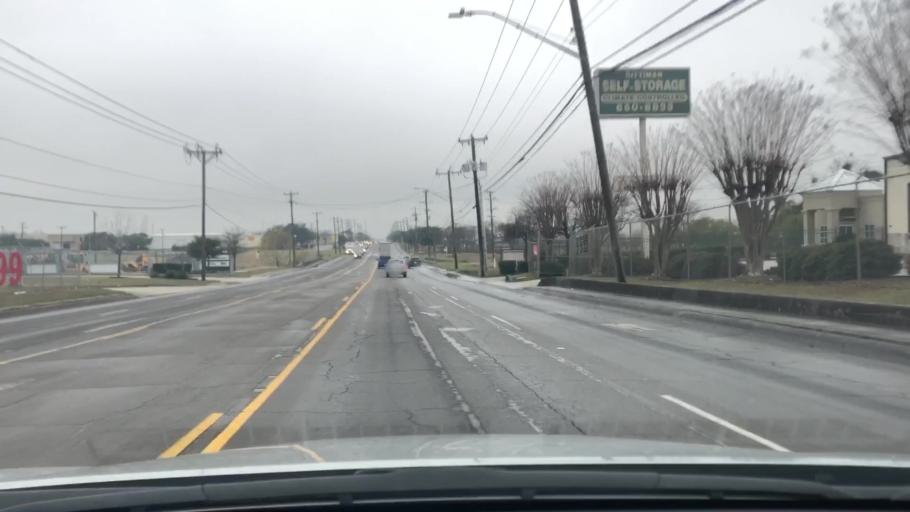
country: US
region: Texas
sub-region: Bexar County
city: Kirby
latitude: 29.4838
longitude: -98.3798
